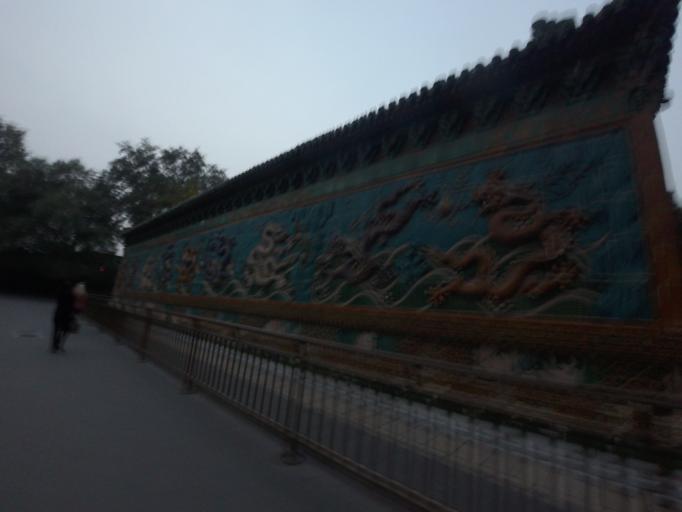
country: CN
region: Beijing
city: Jingshan
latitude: 39.9304
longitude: 116.3815
